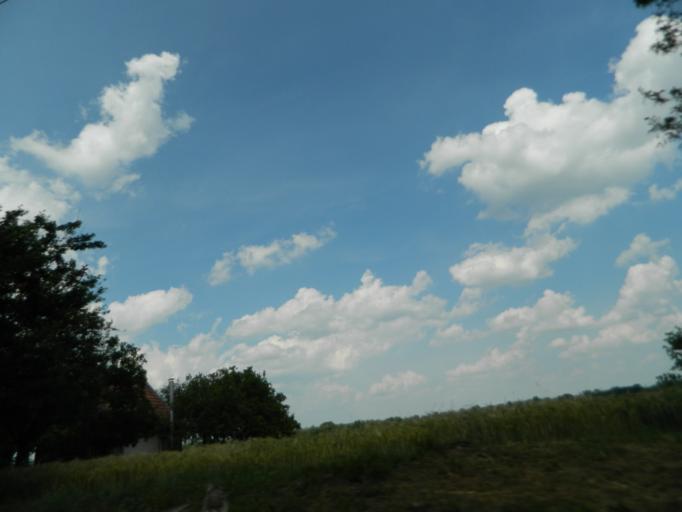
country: HU
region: Somogy
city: Balatonfoldvar
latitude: 46.7888
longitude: 17.9436
